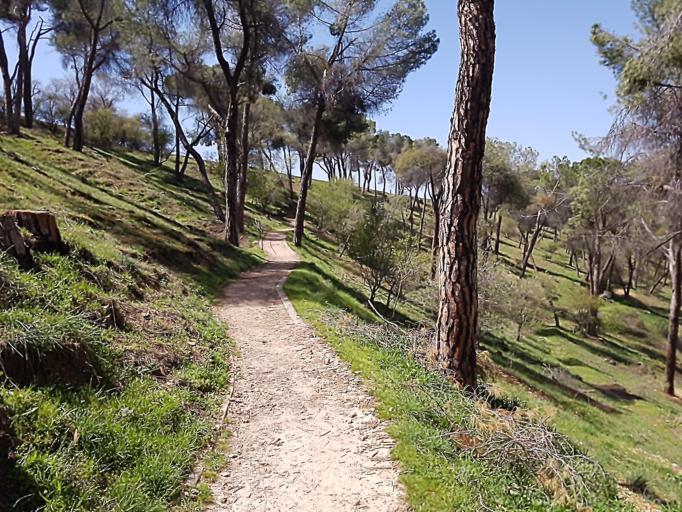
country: ES
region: Castille and Leon
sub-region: Provincia de Segovia
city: Segovia
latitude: 40.9488
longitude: -4.1285
